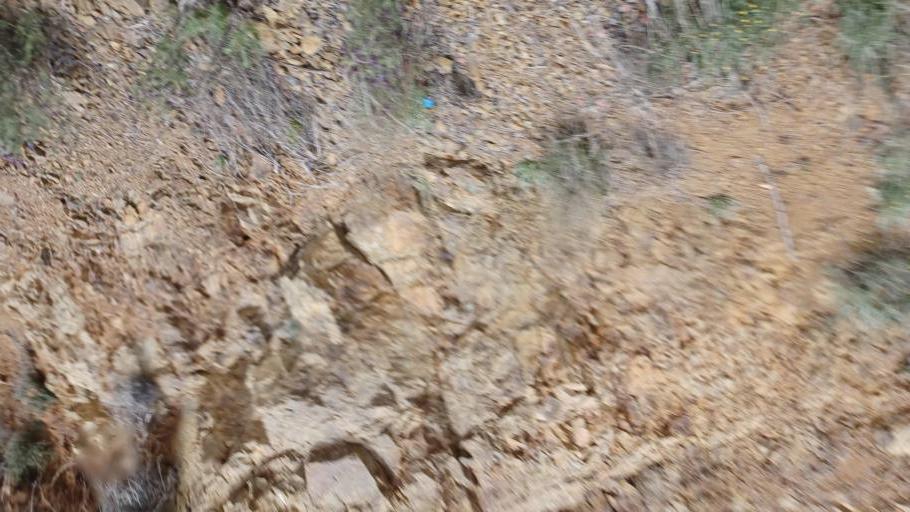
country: CY
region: Limassol
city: Parekklisha
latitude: 34.8532
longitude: 33.1079
